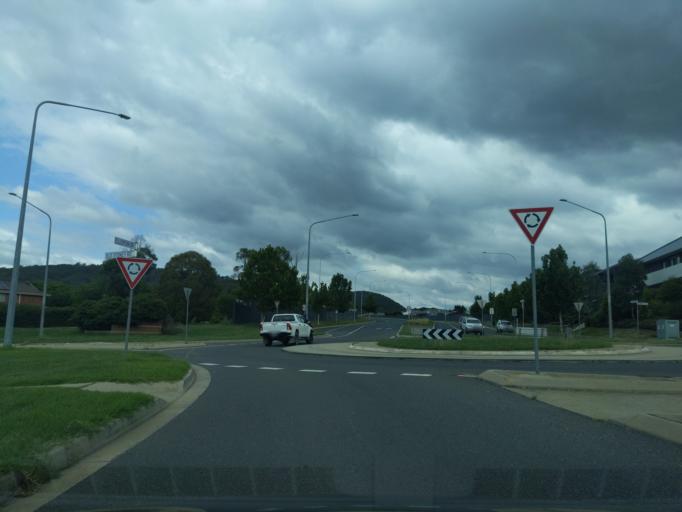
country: AU
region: New South Wales
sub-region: Queanbeyan
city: Queanbeyan
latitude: -35.3505
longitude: 149.2467
